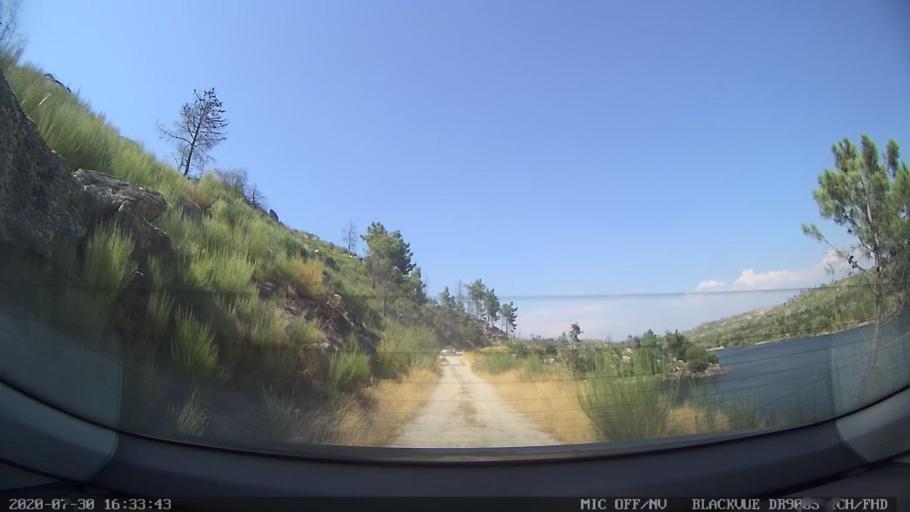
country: PT
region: Vila Real
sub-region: Sabrosa
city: Sabrosa
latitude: 41.3093
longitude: -7.4922
